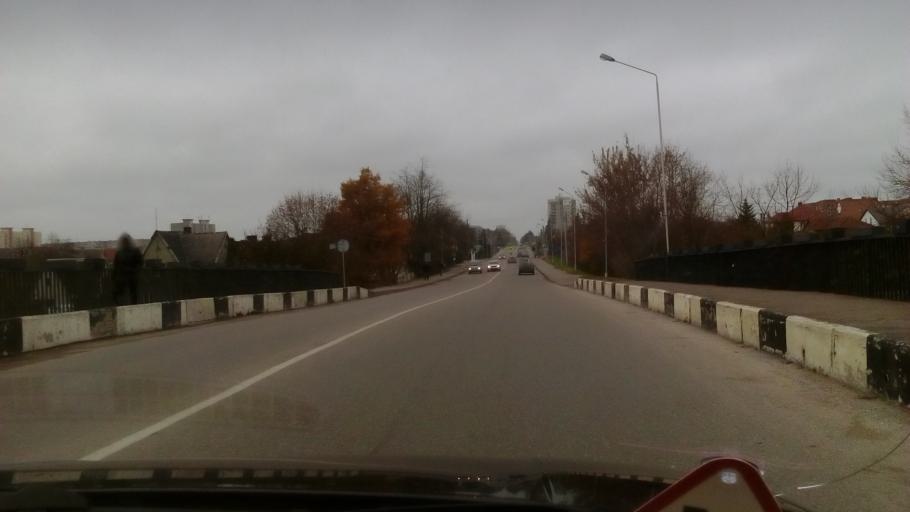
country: LT
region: Marijampoles apskritis
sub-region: Marijampole Municipality
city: Marijampole
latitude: 54.5593
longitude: 23.3454
